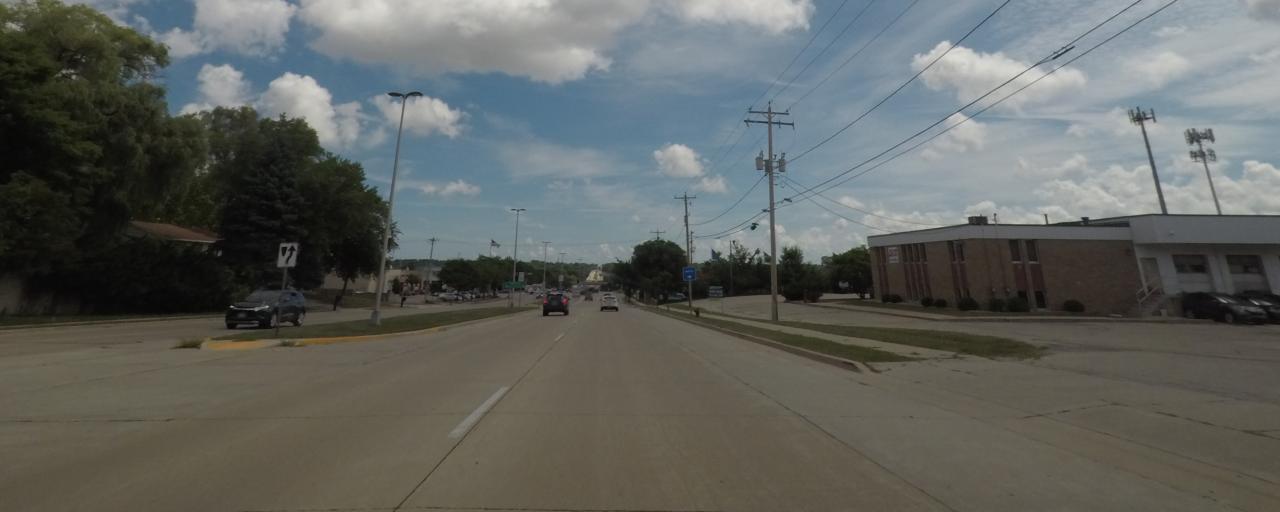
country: US
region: Wisconsin
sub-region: Milwaukee County
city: Hales Corners
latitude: 42.9591
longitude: -88.0505
